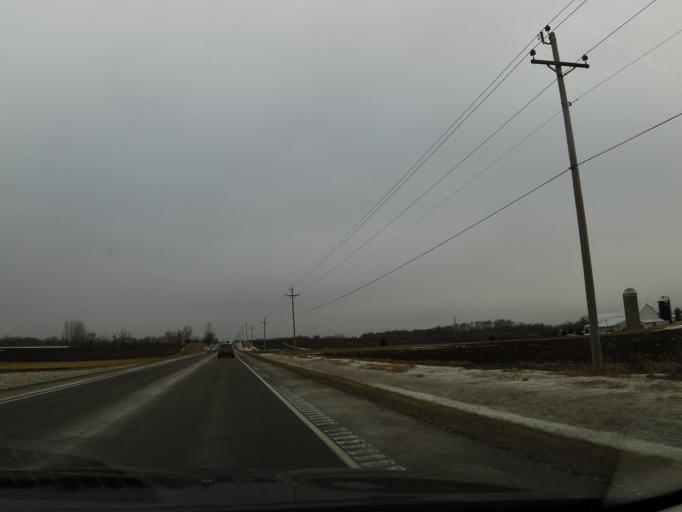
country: US
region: Minnesota
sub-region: Carver County
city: Young America (historical)
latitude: 44.7678
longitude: -93.8621
